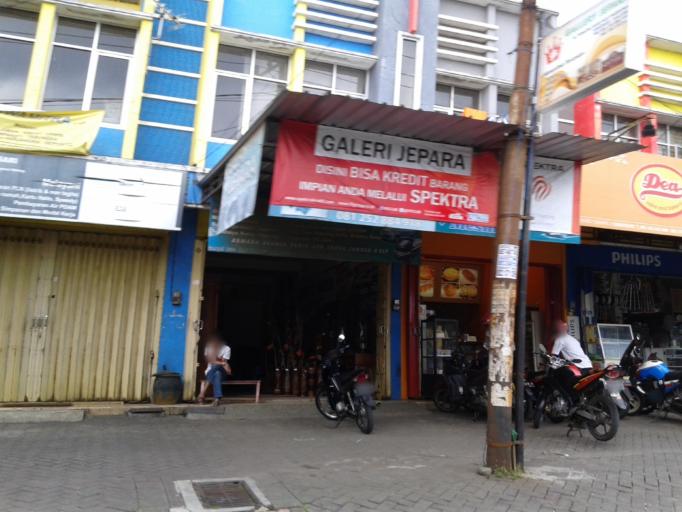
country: ID
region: East Java
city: Singosari
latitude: -7.8939
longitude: 112.6639
